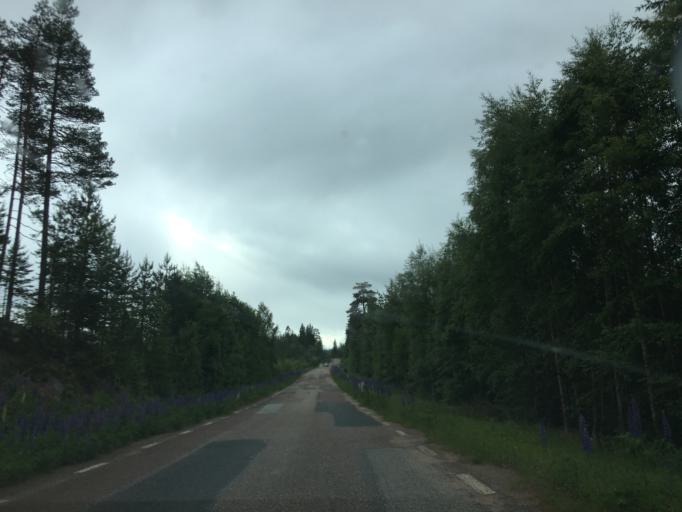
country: SE
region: OErebro
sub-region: Hallefors Kommun
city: Haellefors
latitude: 60.0664
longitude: 14.4935
